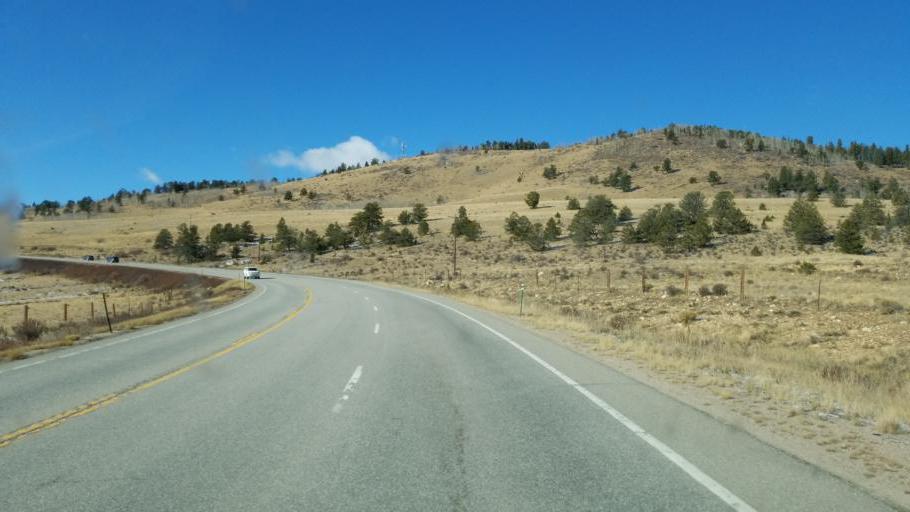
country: US
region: Colorado
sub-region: Park County
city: Fairplay
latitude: 39.2764
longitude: -105.9506
